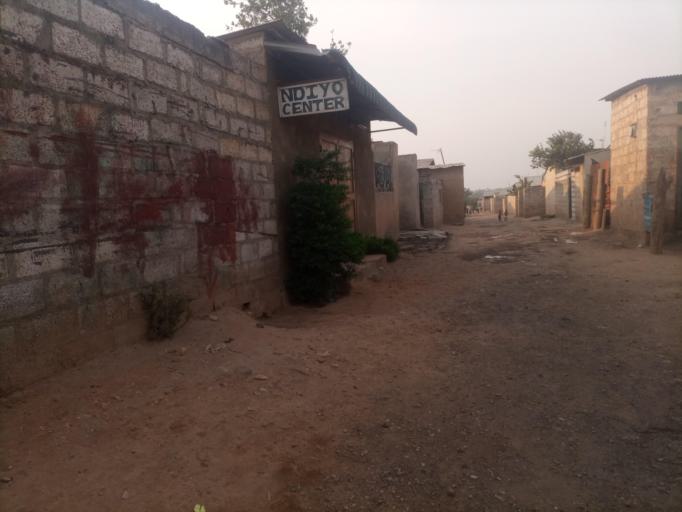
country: ZM
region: Lusaka
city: Lusaka
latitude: -15.3962
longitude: 28.3776
